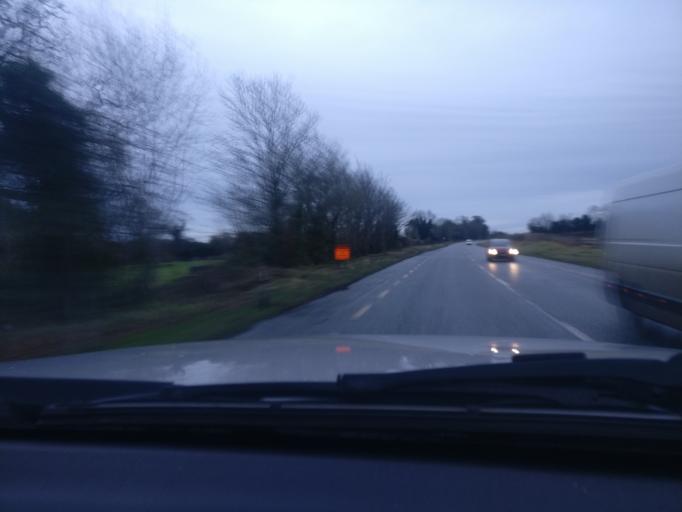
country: IE
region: Leinster
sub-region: An Mhi
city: Navan
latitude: 53.6690
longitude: -6.7322
